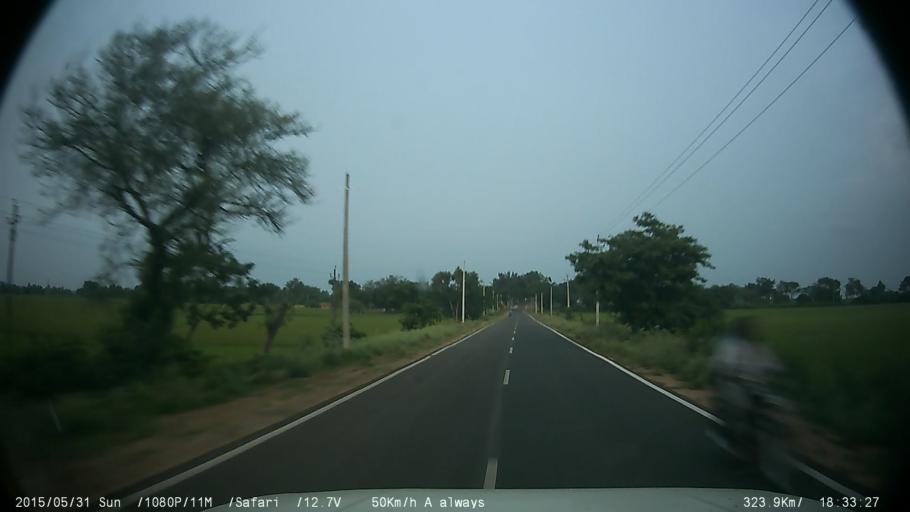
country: IN
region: Karnataka
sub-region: Mysore
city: Nanjangud
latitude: 12.1392
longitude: 76.7512
